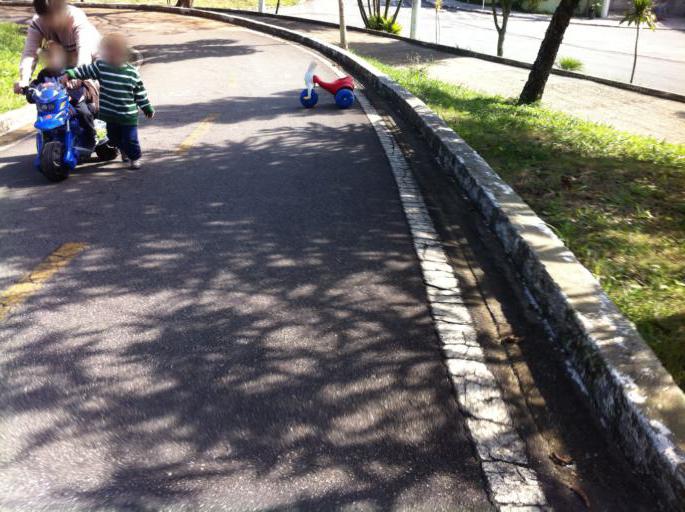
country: BR
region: Sao Paulo
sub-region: Sao Bernardo Do Campo
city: Sao Bernardo do Campo
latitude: -23.7085
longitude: -46.5812
